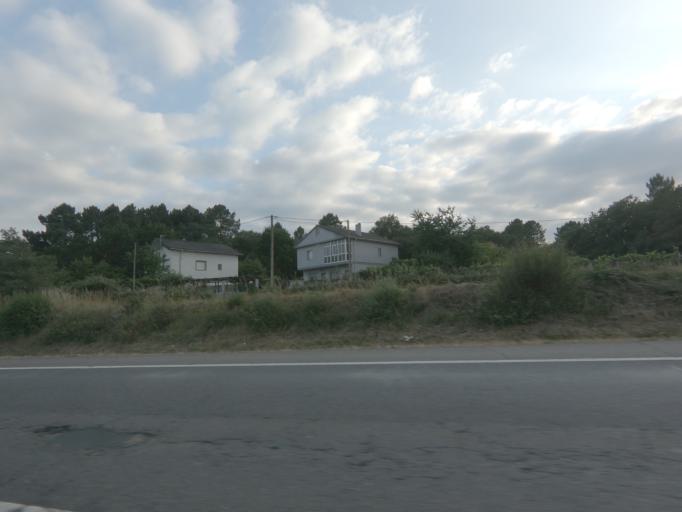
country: ES
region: Galicia
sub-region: Provincia de Ourense
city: Taboadela
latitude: 42.2657
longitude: -7.8359
